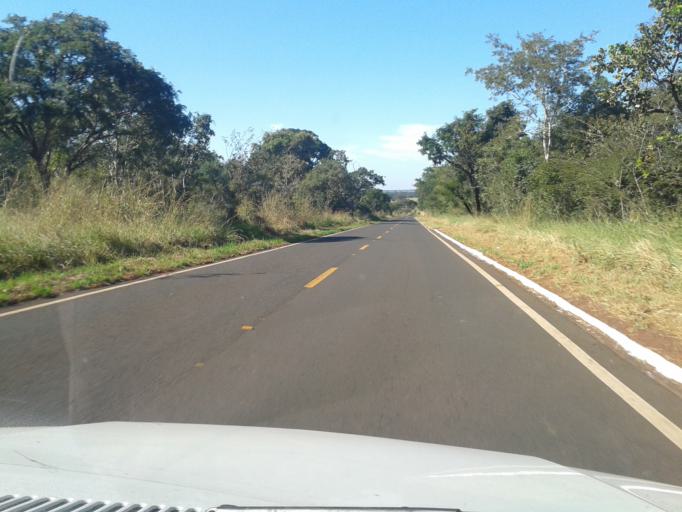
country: BR
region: Minas Gerais
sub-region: Ituiutaba
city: Ituiutaba
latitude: -19.0287
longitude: -49.7710
